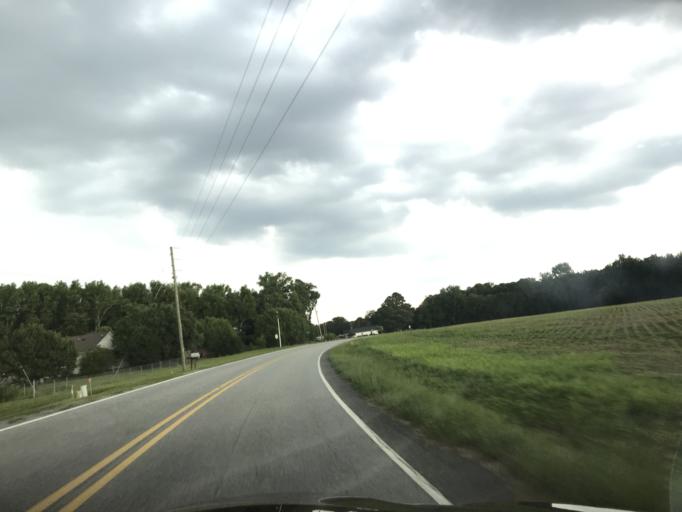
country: US
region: North Carolina
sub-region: Johnston County
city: Wilsons Mills
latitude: 35.5421
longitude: -78.4216
